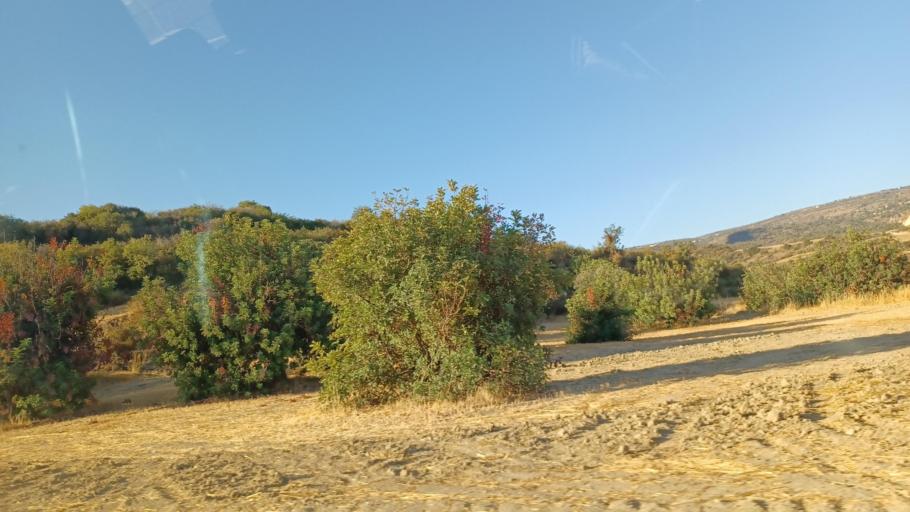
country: CY
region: Pafos
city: Polis
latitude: 34.9767
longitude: 32.4568
